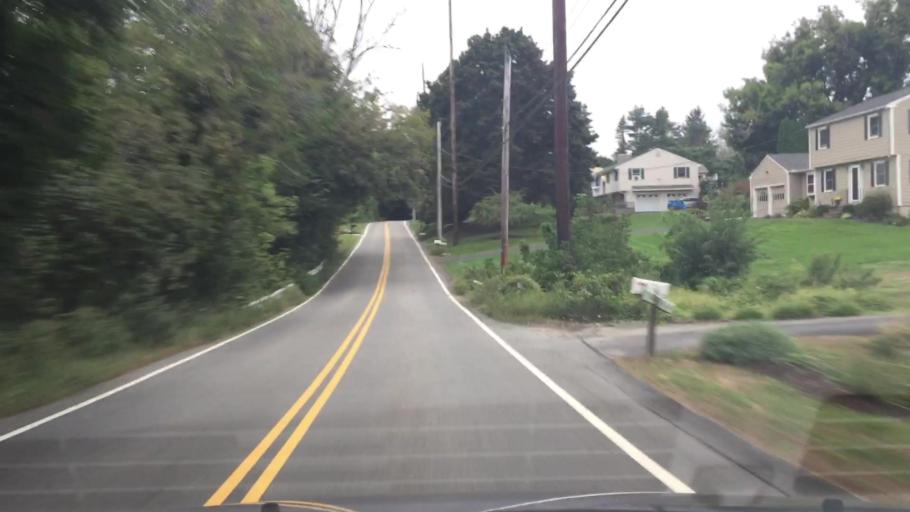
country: US
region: Massachusetts
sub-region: Essex County
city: North Andover
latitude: 42.7304
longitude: -71.1038
